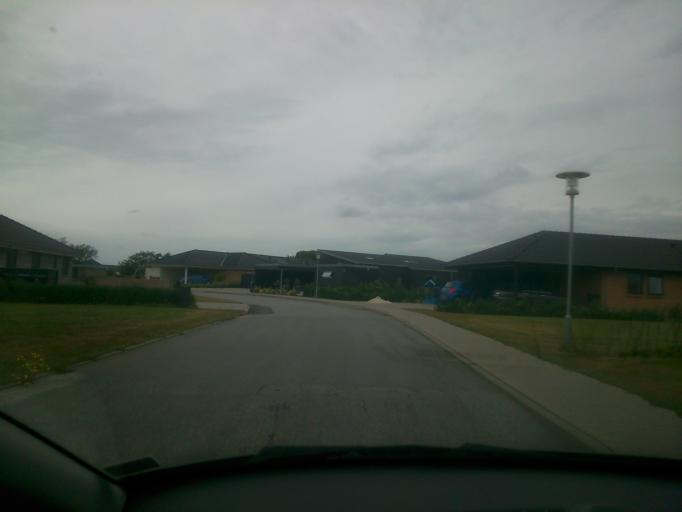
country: DK
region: South Denmark
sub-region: Esbjerg Kommune
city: Esbjerg
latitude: 55.5281
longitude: 8.4253
